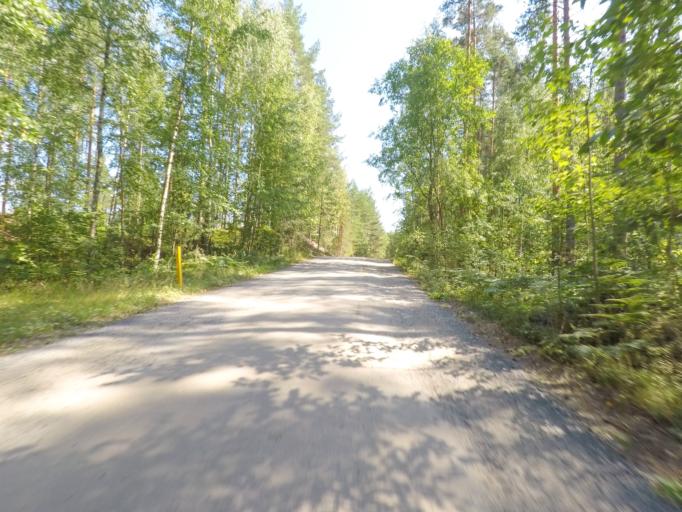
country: FI
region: Southern Savonia
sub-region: Mikkeli
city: Puumala
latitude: 61.4229
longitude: 28.0399
